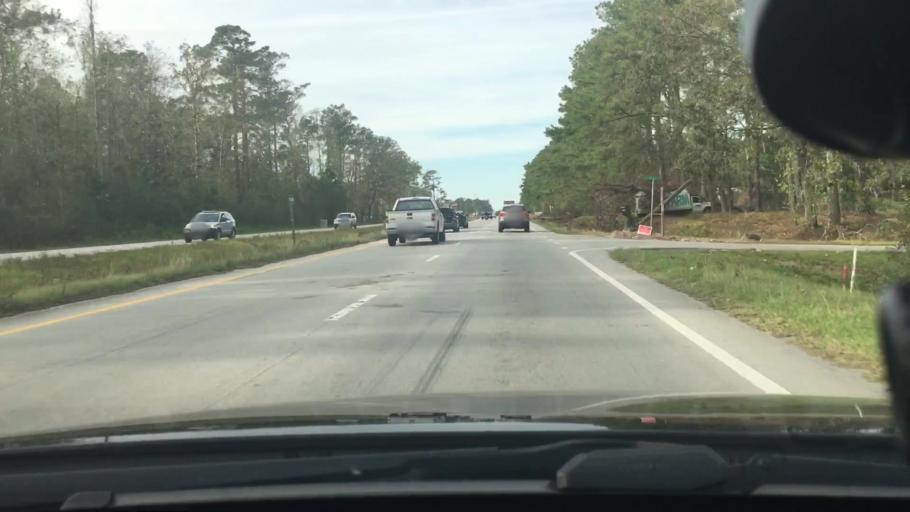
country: US
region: North Carolina
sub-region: Craven County
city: James City
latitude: 35.0424
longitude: -77.0096
